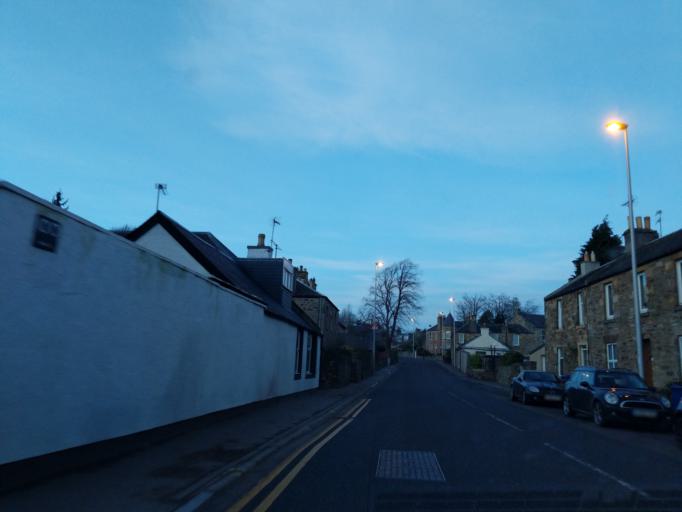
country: GB
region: Scotland
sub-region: Midlothian
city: Bonnyrigg
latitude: 55.8782
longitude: -3.1079
